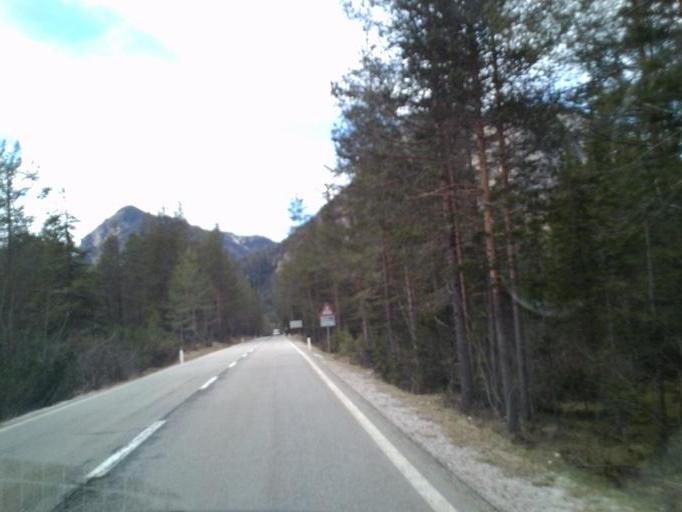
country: IT
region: Veneto
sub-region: Provincia di Belluno
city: Cortina d'Ampezzo
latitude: 46.6129
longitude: 12.2262
